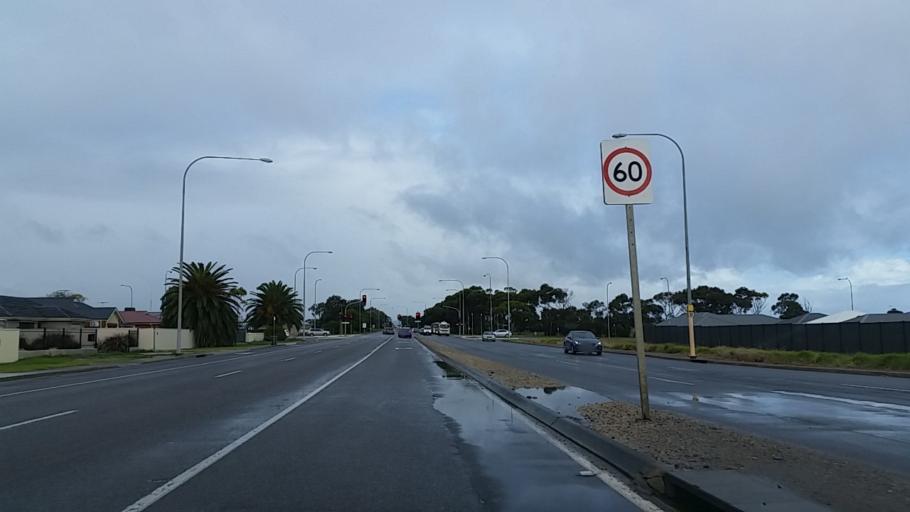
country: AU
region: South Australia
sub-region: Onkaparinga
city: Noarlunga
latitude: -35.1893
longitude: 138.4901
